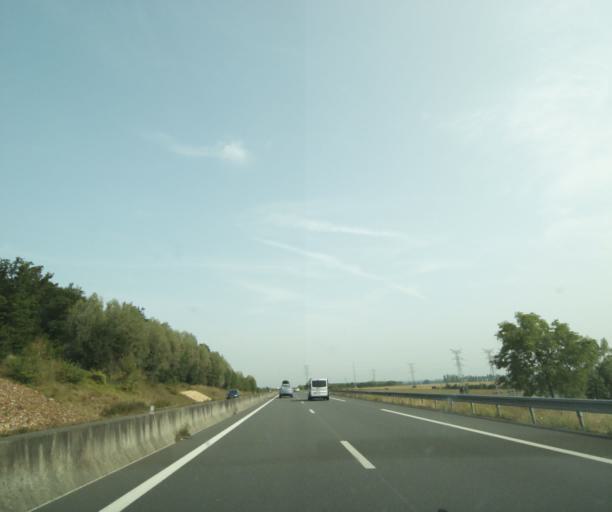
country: FR
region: Pays de la Loire
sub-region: Departement de la Sarthe
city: Arconnay
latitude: 48.3736
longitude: 0.1030
